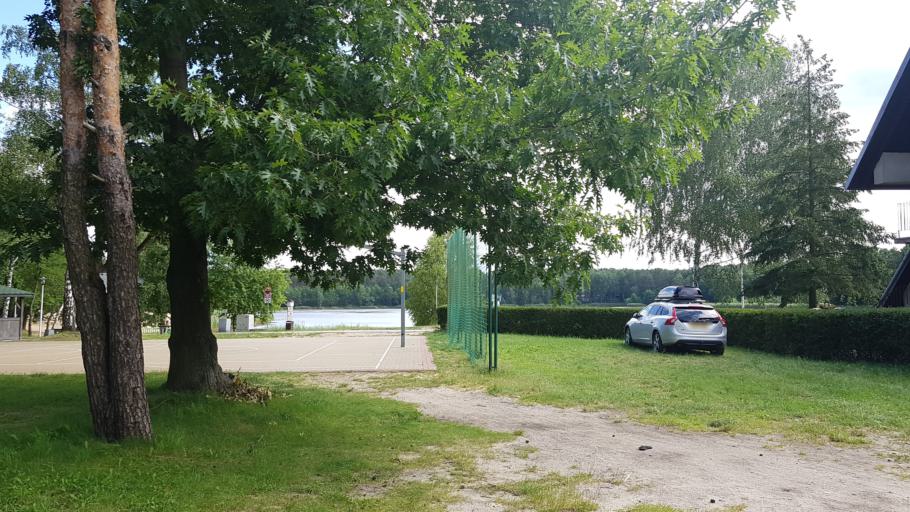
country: PL
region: Opole Voivodeship
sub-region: Powiat opolski
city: Chrzastowice
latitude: 50.7127
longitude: 18.1028
